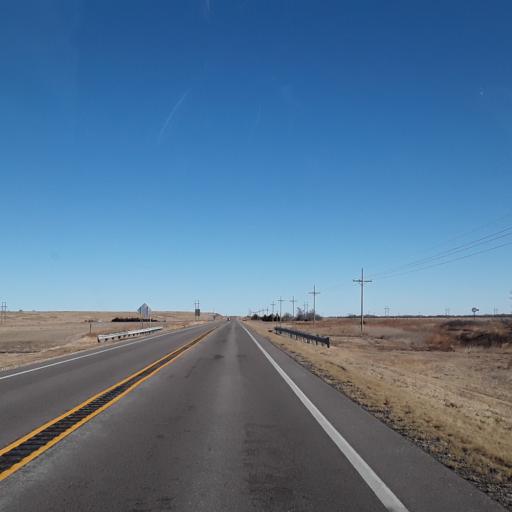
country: US
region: Kansas
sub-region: Pawnee County
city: Larned
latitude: 38.0829
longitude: -99.2326
